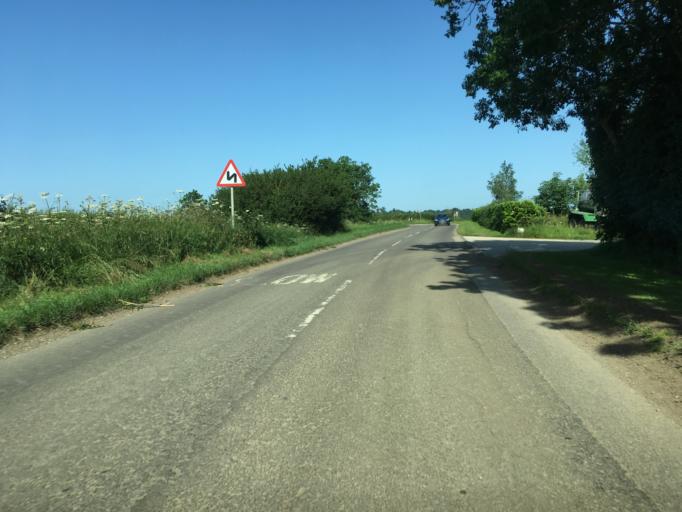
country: GB
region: England
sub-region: Buckinghamshire
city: Steeple Claydon
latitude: 51.9335
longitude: -1.0028
